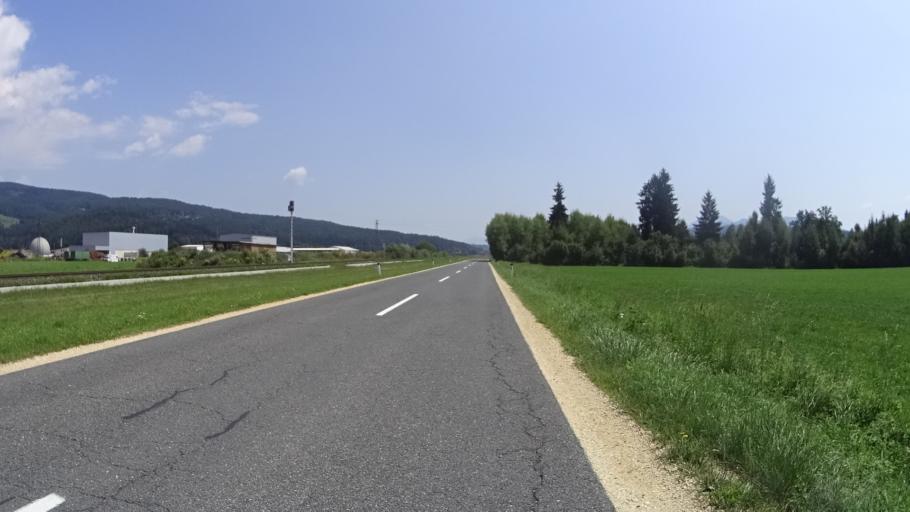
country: AT
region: Carinthia
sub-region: Politischer Bezirk Volkermarkt
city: Bleiburg/Pliberk
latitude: 46.5725
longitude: 14.7951
